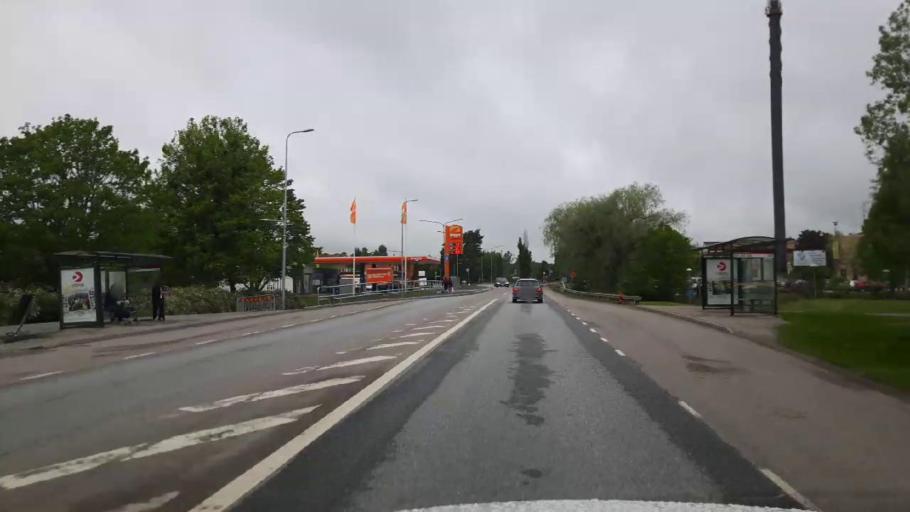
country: SE
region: Stockholm
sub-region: Upplands-Bro Kommun
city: Bro
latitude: 59.5143
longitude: 17.6430
